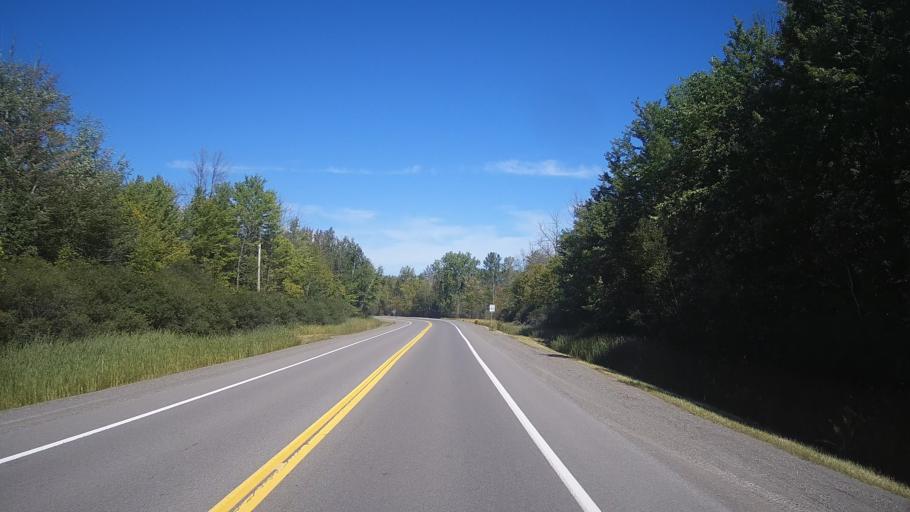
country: CA
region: Ontario
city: Bells Corners
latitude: 45.0756
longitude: -75.6478
